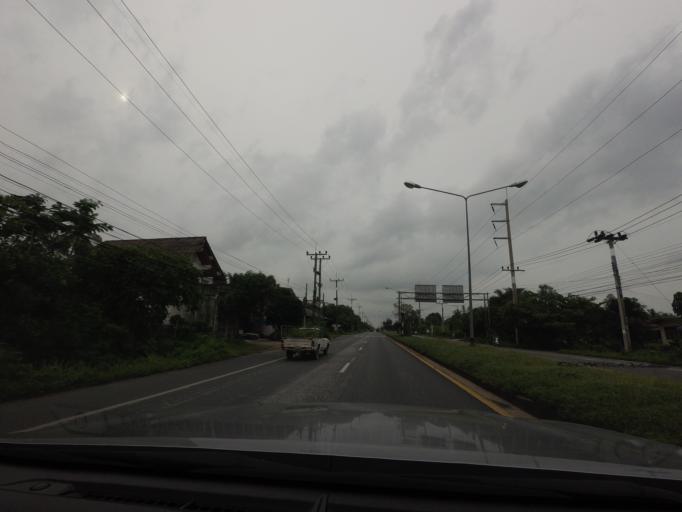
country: TH
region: Songkhla
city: Sathing Phra
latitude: 7.3628
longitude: 100.4807
